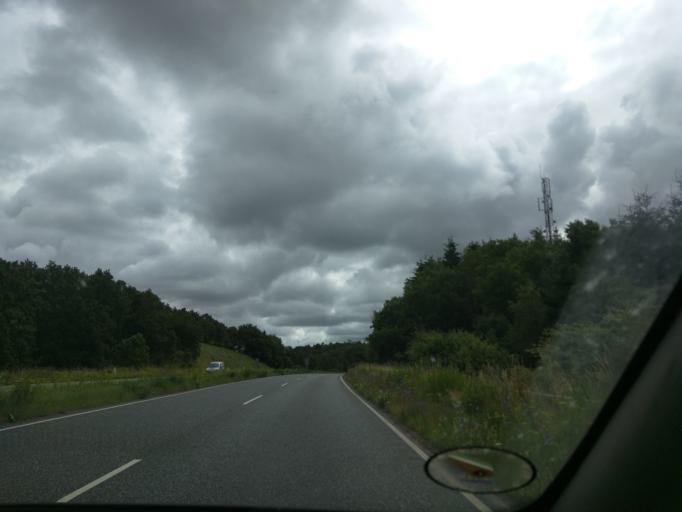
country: DK
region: Zealand
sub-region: Holbaek Kommune
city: Jyderup
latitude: 55.6699
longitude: 11.3563
